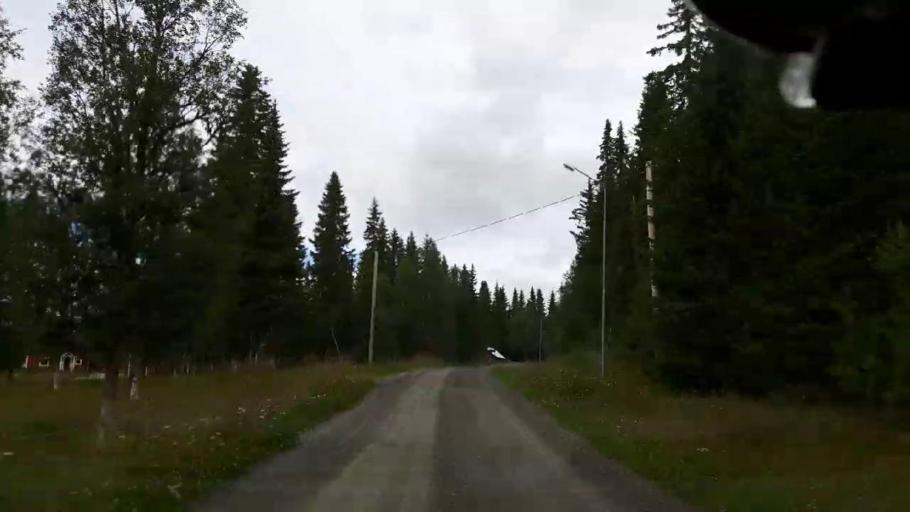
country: SE
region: Jaemtland
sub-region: Krokoms Kommun
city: Valla
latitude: 63.7065
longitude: 13.8660
